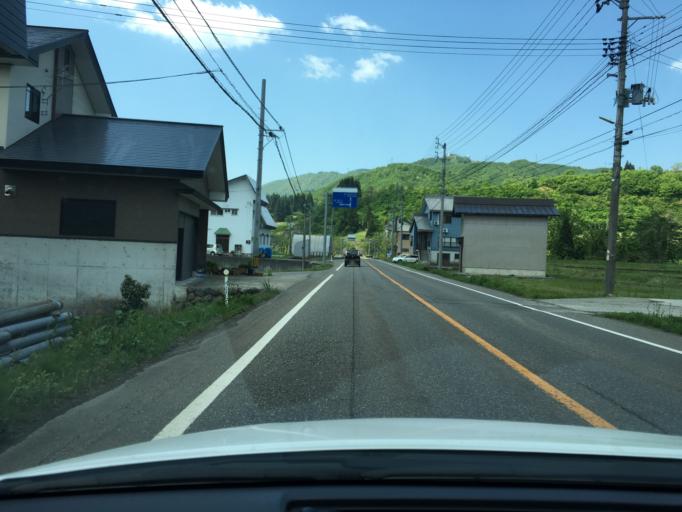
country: JP
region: Niigata
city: Tochio-honcho
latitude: 37.3345
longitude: 139.0319
